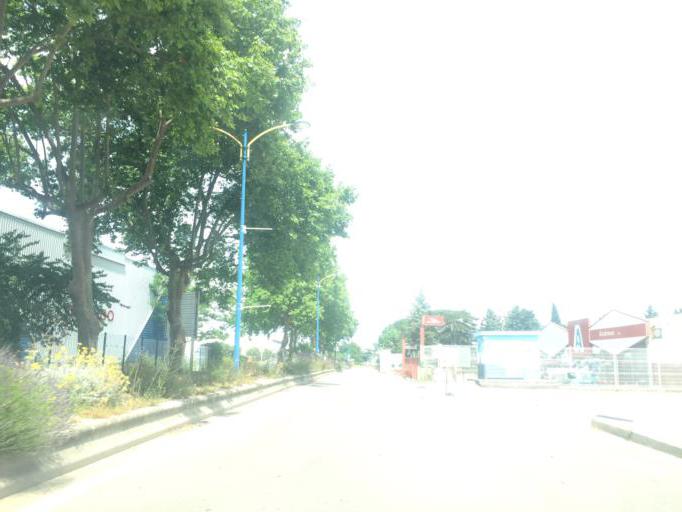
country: FR
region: Languedoc-Roussillon
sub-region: Departement du Gard
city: Pont-Saint-Esprit
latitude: 44.2417
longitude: 4.6411
